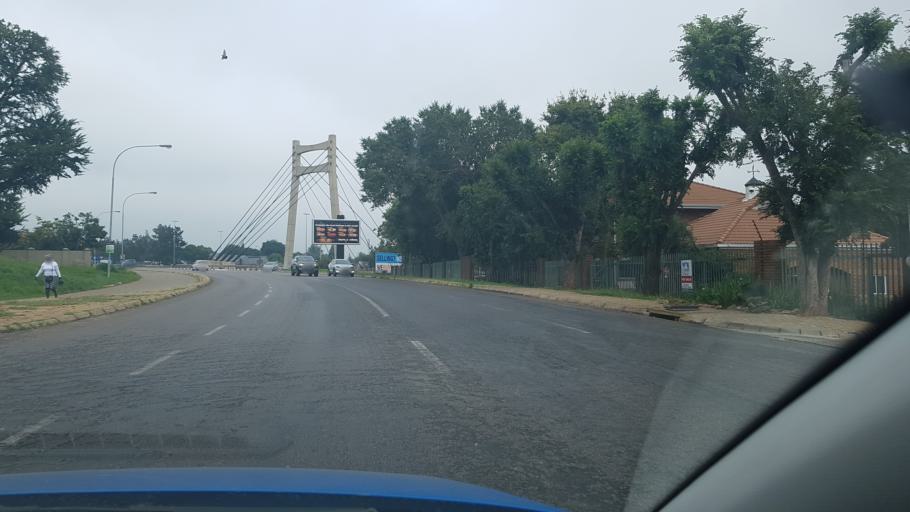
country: ZA
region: Gauteng
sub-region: Ekurhuleni Metropolitan Municipality
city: Germiston
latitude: -26.1659
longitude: 28.1475
